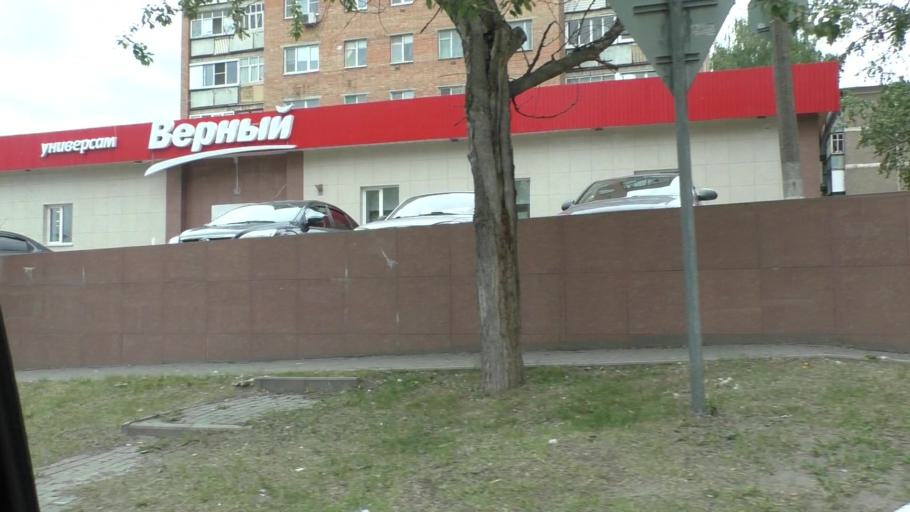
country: RU
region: Moskovskaya
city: Yegor'yevsk
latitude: 55.3664
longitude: 39.0574
